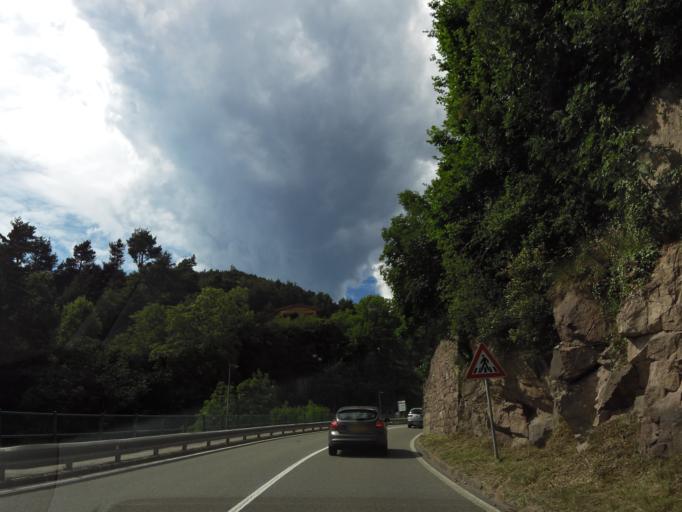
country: IT
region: Trentino-Alto Adige
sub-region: Bolzano
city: Siusi
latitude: 46.5498
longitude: 11.5556
